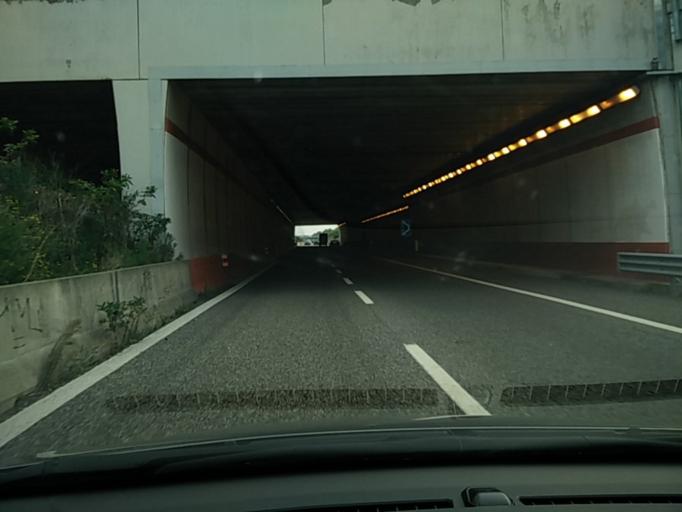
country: IT
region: Lombardy
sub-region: Provincia di Varese
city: Vizzola Ticino
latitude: 45.6118
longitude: 8.7096
